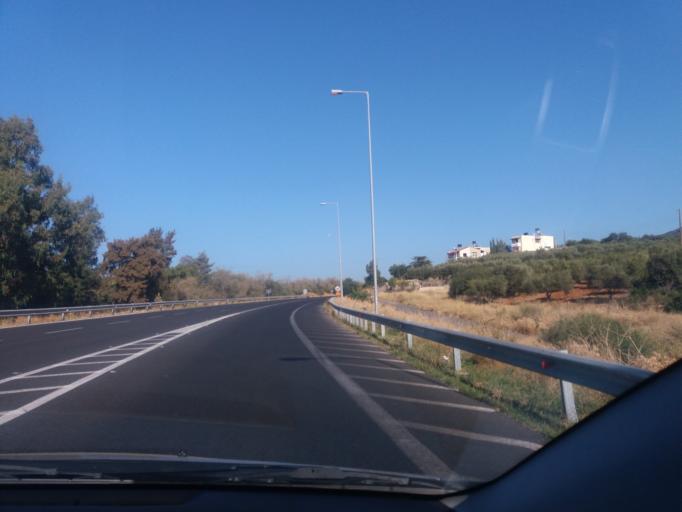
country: GR
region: Crete
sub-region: Nomos Lasithiou
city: Sision
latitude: 35.2913
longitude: 25.5123
